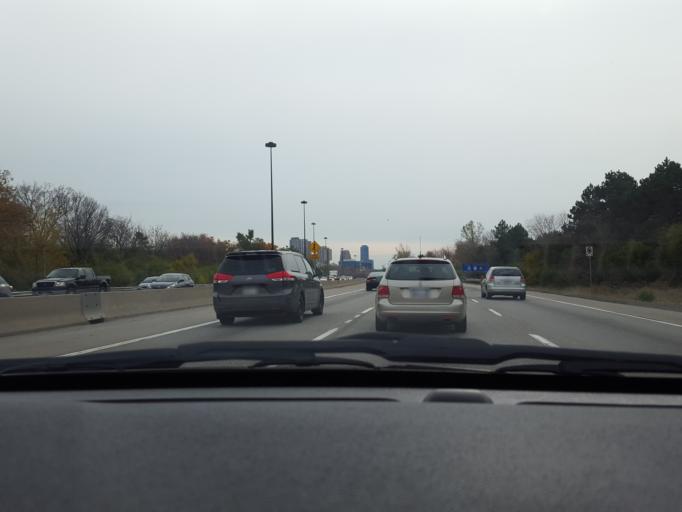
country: CA
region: Ontario
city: Willowdale
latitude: 43.7480
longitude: -79.3335
